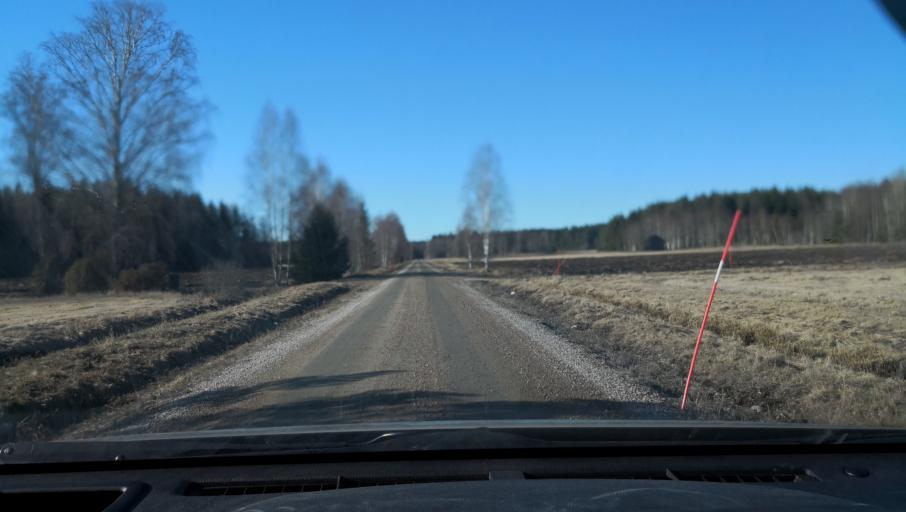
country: SE
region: Vaestmanland
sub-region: Sala Kommun
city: Sala
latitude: 60.1278
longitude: 16.6544
